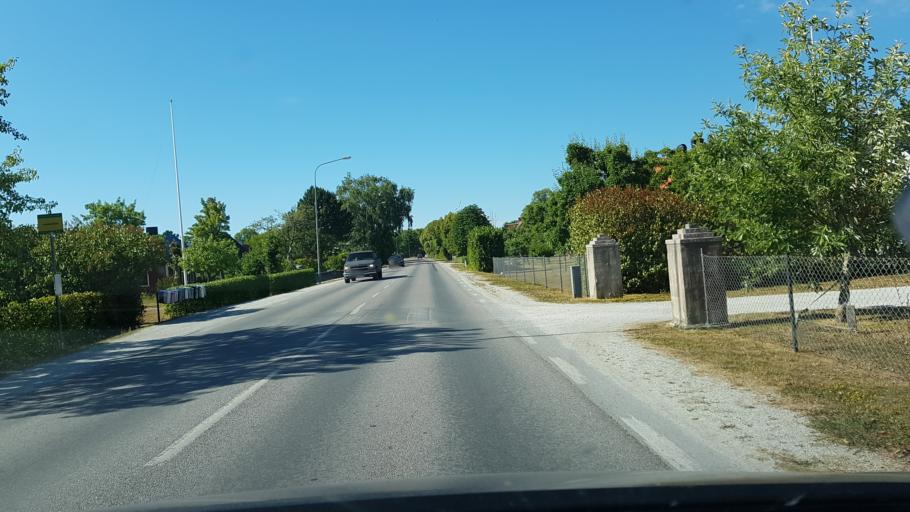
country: SE
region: Gotland
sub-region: Gotland
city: Klintehamn
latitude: 57.4350
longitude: 18.1460
